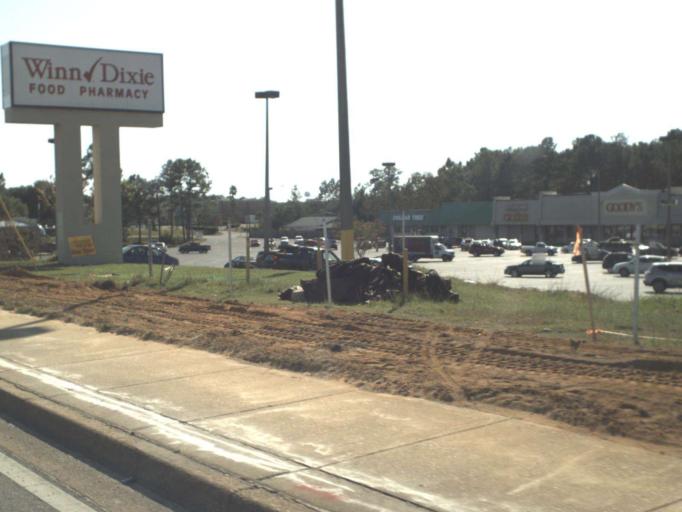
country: US
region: Florida
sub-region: Walton County
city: DeFuniak Springs
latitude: 30.7079
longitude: -86.1229
